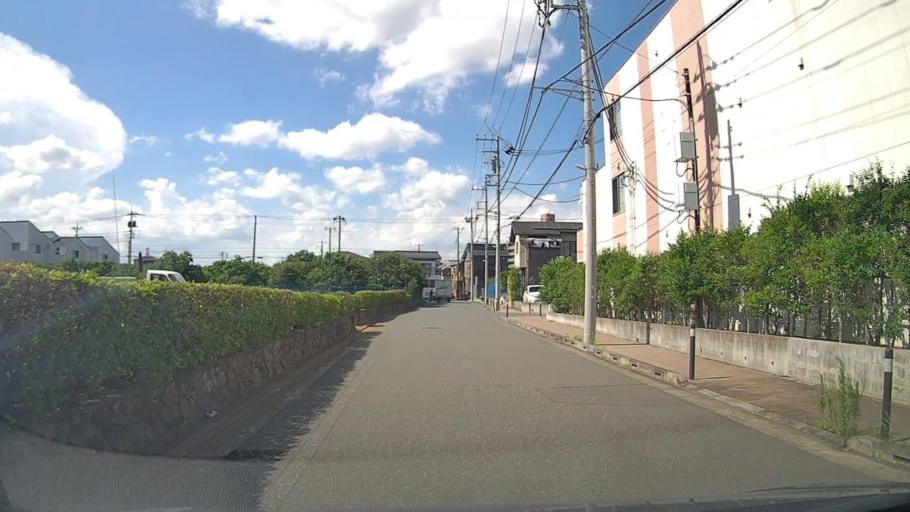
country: JP
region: Saitama
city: Wako
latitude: 35.7690
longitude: 139.6035
